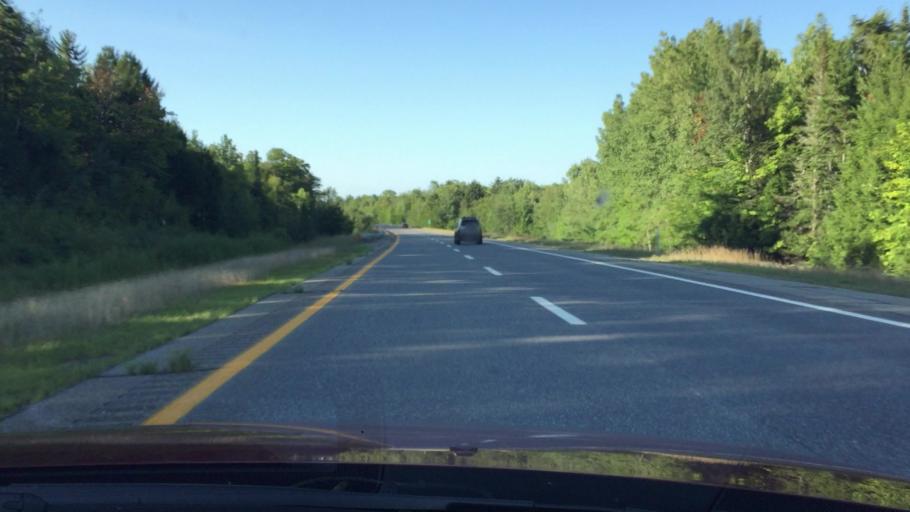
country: US
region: Maine
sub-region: Penobscot County
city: Lincoln
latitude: 45.4235
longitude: -68.5893
